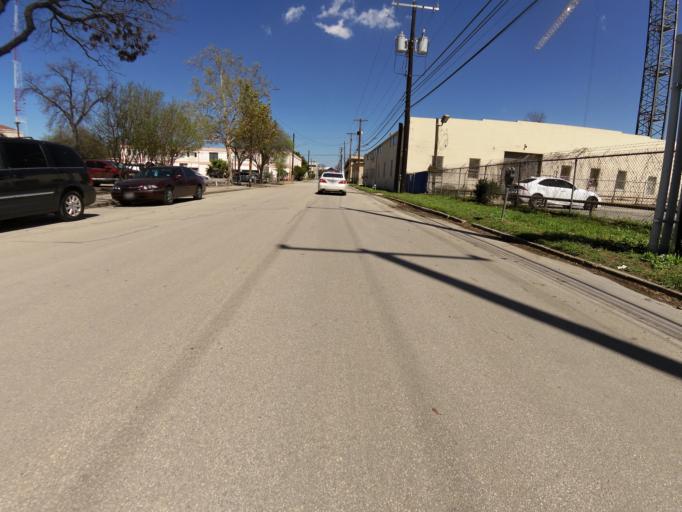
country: US
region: Texas
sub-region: Bexar County
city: San Antonio
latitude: 29.4328
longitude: -98.4841
